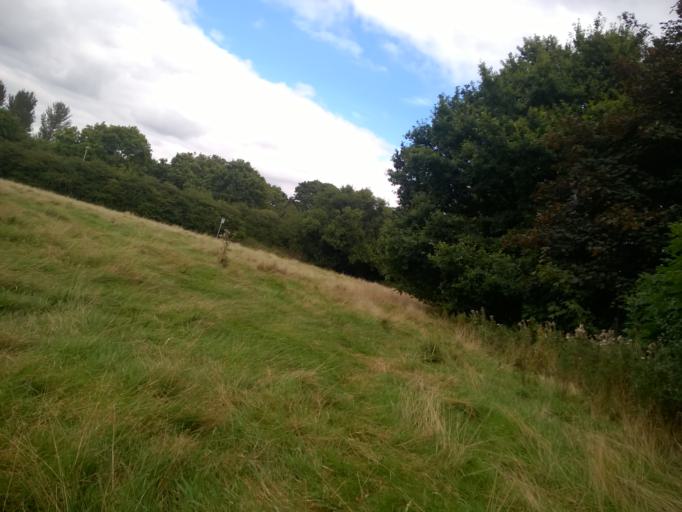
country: GB
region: England
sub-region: Leicestershire
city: Glenfield
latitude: 52.6356
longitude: -1.2093
